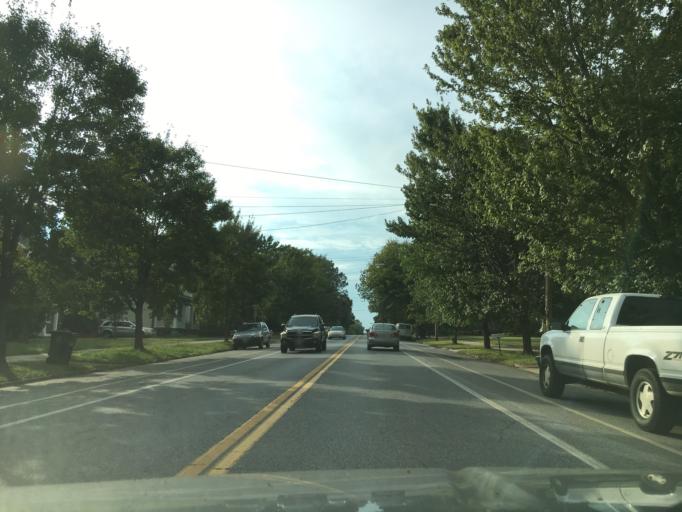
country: US
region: Virginia
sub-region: City of Lynchburg
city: Lynchburg
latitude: 37.4318
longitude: -79.1557
